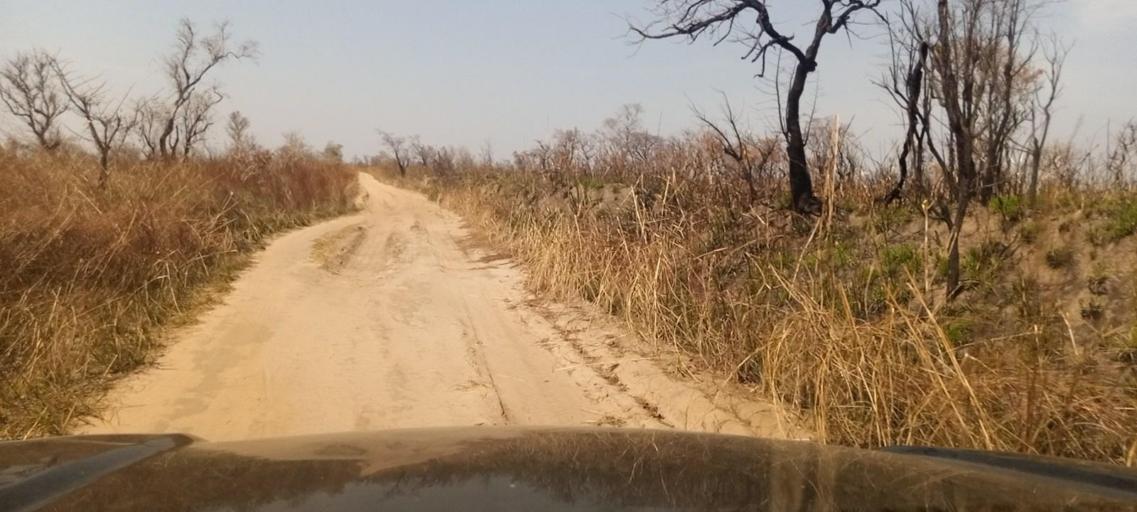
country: CD
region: Kasai-Oriental
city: Kabinda
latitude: -5.7935
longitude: 25.0370
